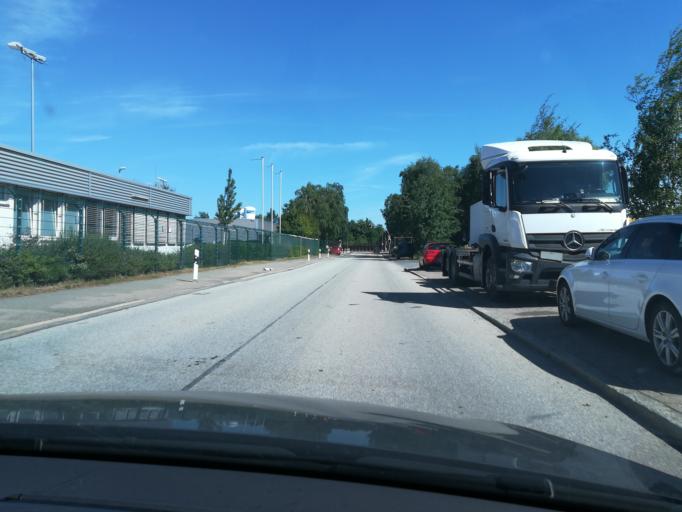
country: DE
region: Hamburg
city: Rothenburgsort
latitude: 53.5123
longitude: 10.0505
